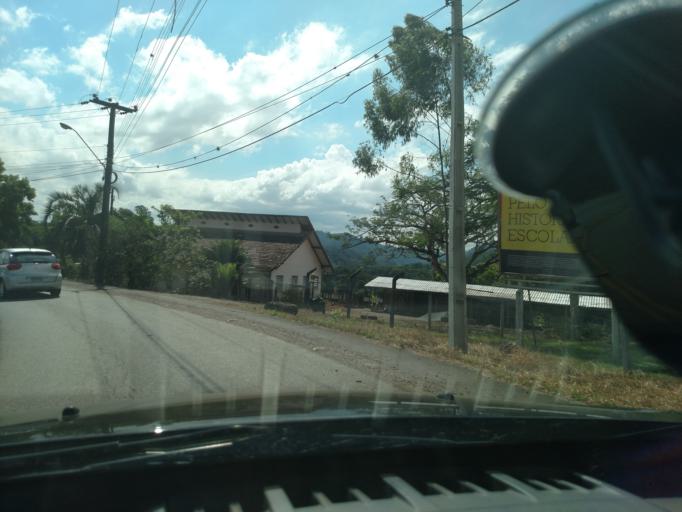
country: BR
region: Santa Catarina
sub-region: Indaial
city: Indaial
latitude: -26.8808
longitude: -49.1762
